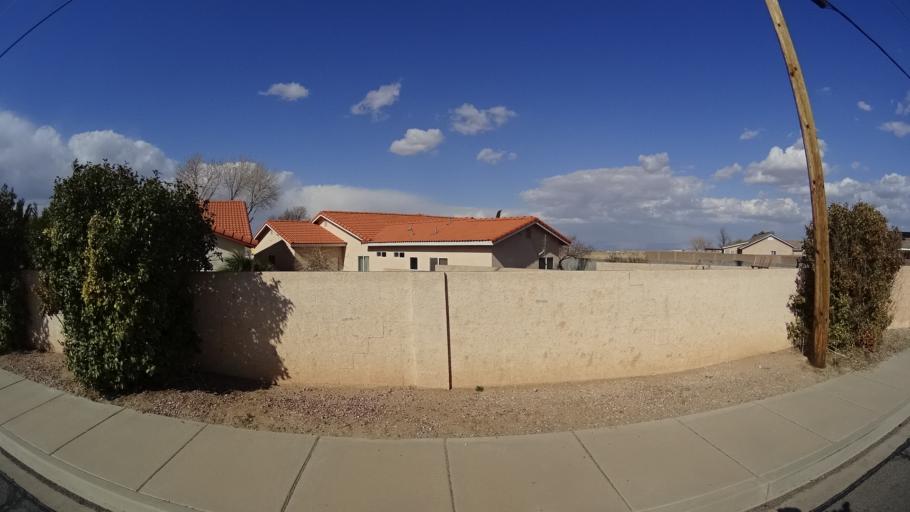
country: US
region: Arizona
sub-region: Mohave County
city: New Kingman-Butler
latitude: 35.2250
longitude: -113.9896
